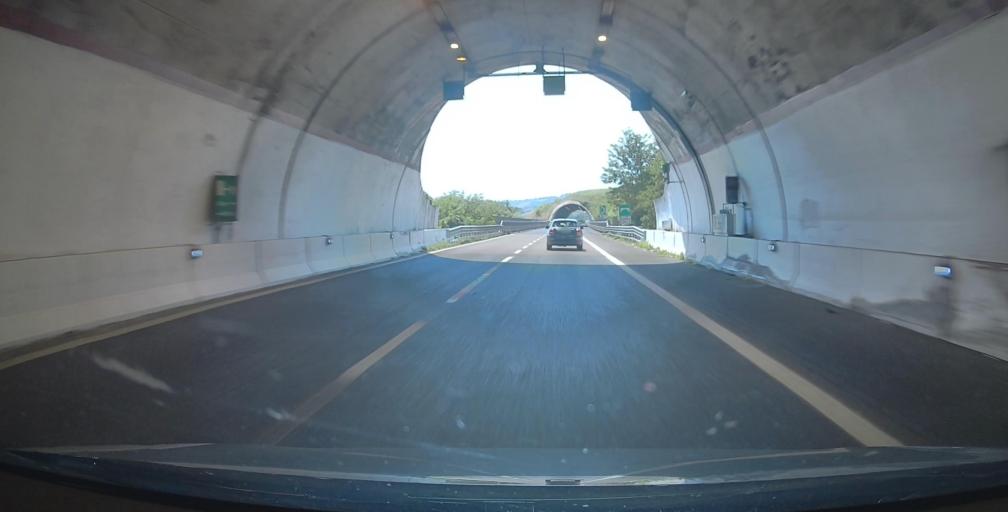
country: IT
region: Calabria
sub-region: Provincia di Vibo-Valentia
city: Francica
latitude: 38.5750
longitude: 16.1119
